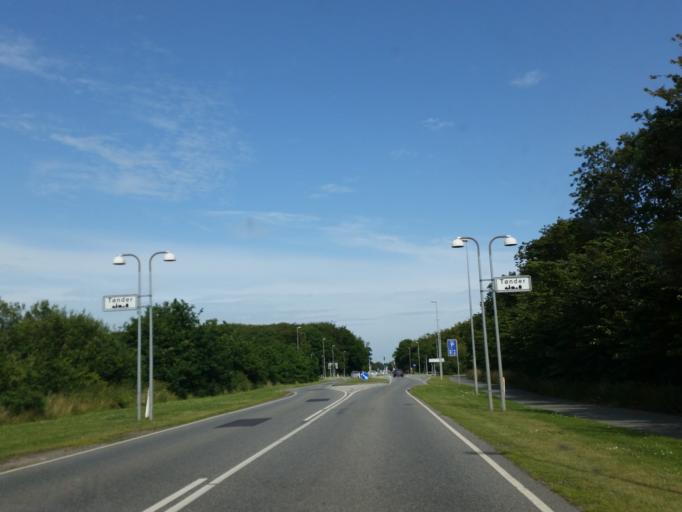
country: DK
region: South Denmark
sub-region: Tonder Kommune
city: Tonder
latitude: 54.9455
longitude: 8.8525
